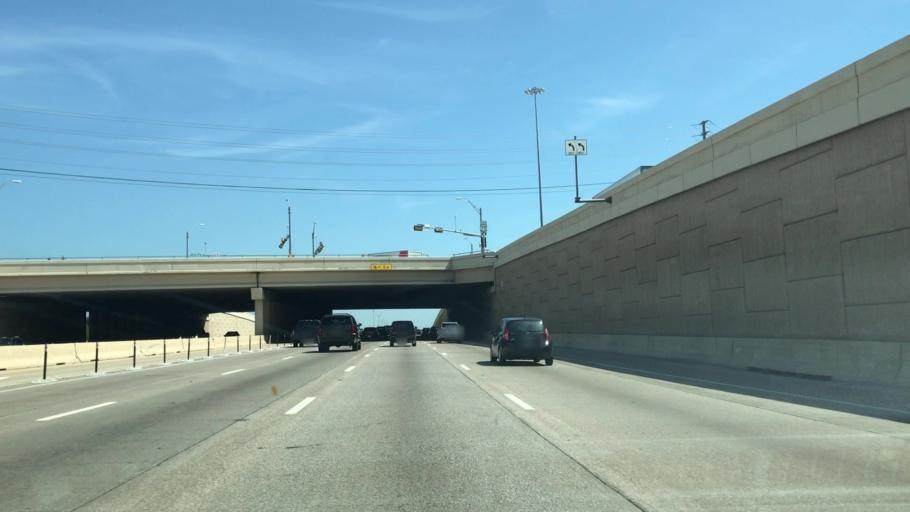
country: US
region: Texas
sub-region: Collin County
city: Plano
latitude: 33.0364
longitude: -96.7049
